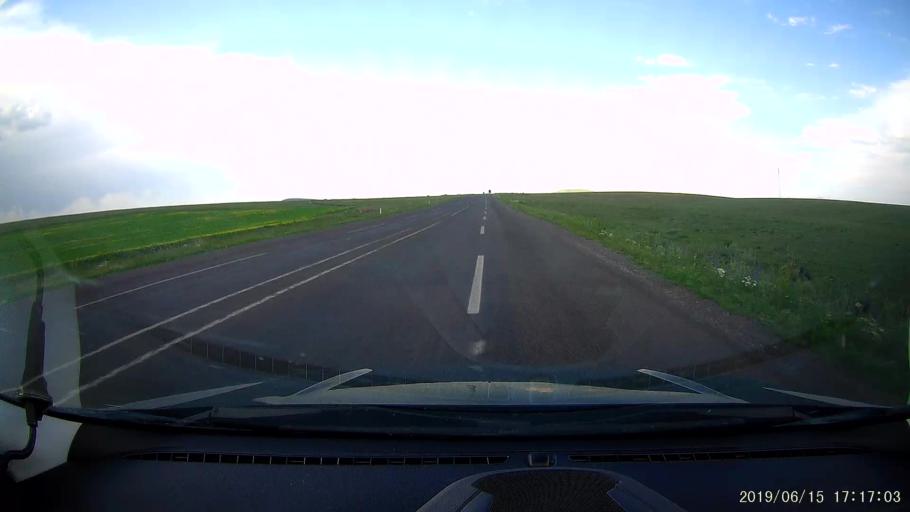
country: TR
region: Kars
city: Kars
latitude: 40.6143
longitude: 43.2304
